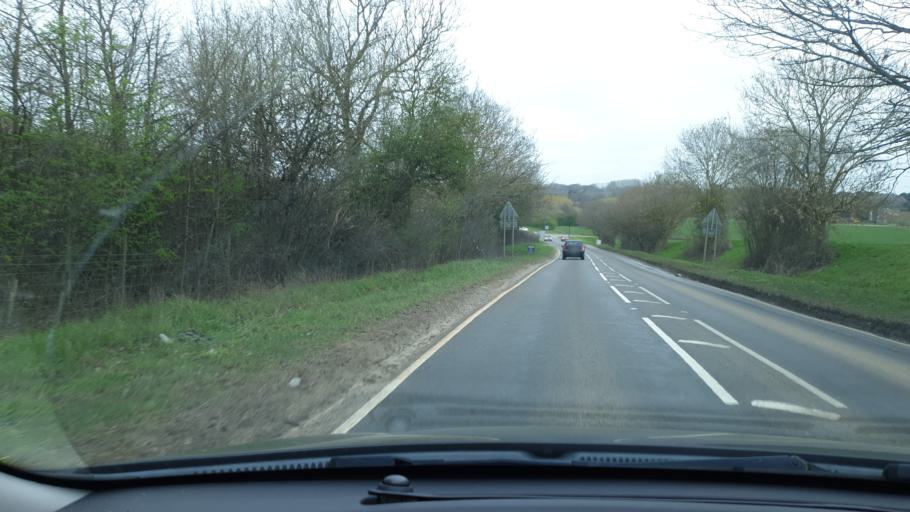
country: GB
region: England
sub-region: Essex
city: Great Horkesley
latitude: 51.9638
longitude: 0.8685
